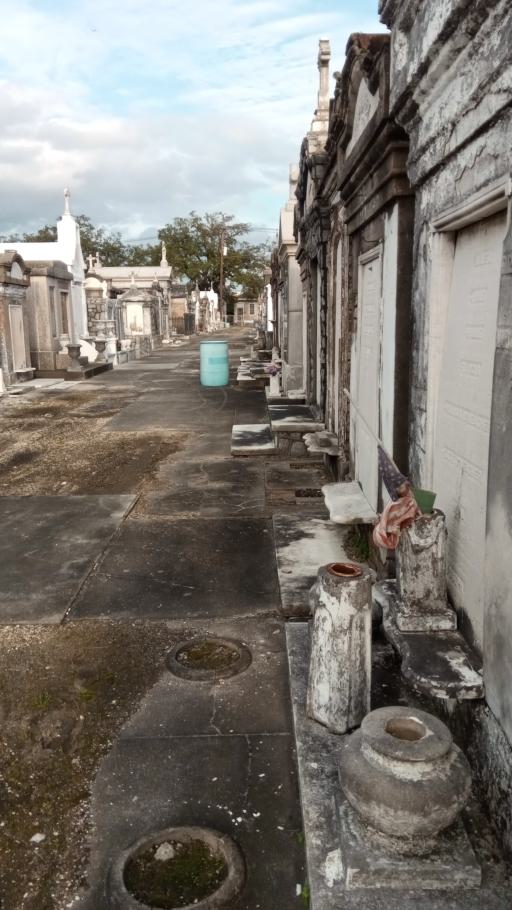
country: US
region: Louisiana
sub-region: Orleans Parish
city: New Orleans
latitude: 29.9359
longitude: -90.0910
